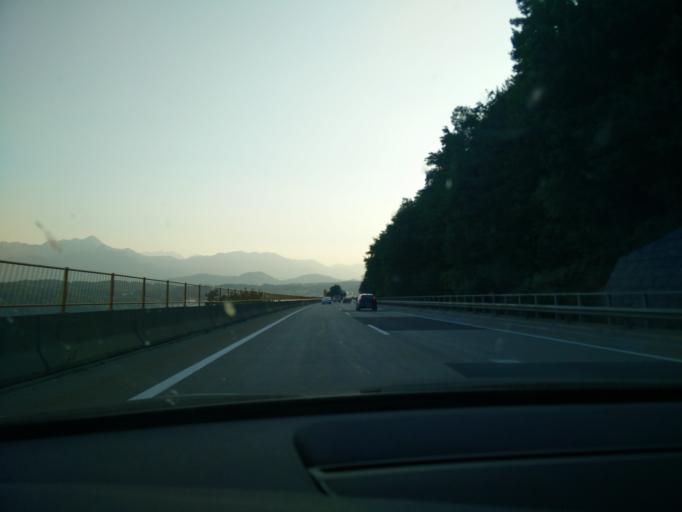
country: AT
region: Carinthia
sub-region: Politischer Bezirk Klagenfurt Land
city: Schiefling am See
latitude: 46.6262
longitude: 14.0835
